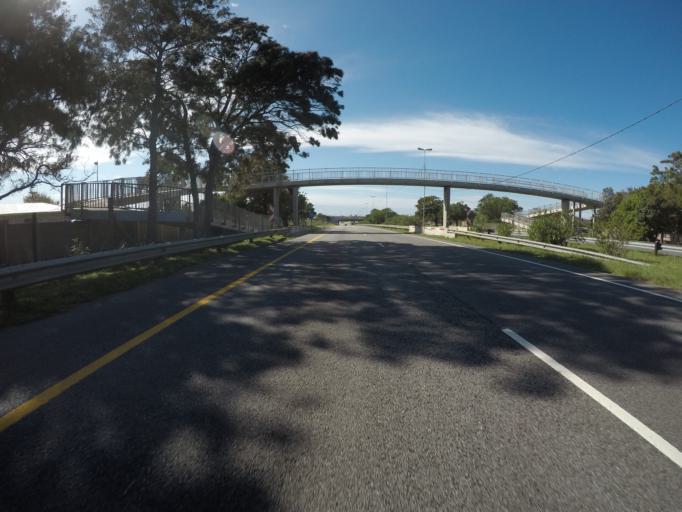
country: ZA
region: Eastern Cape
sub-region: Nelson Mandela Bay Metropolitan Municipality
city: Port Elizabeth
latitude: -33.9471
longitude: 25.5229
